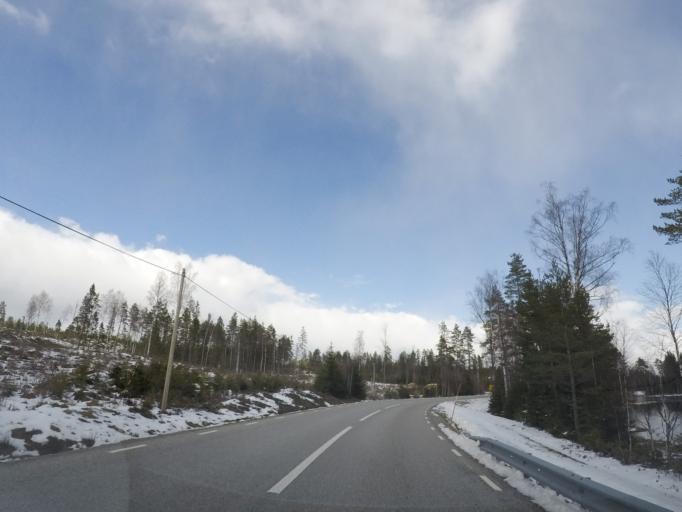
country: SE
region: OErebro
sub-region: Lindesbergs Kommun
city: Stora
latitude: 59.8937
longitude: 15.2609
